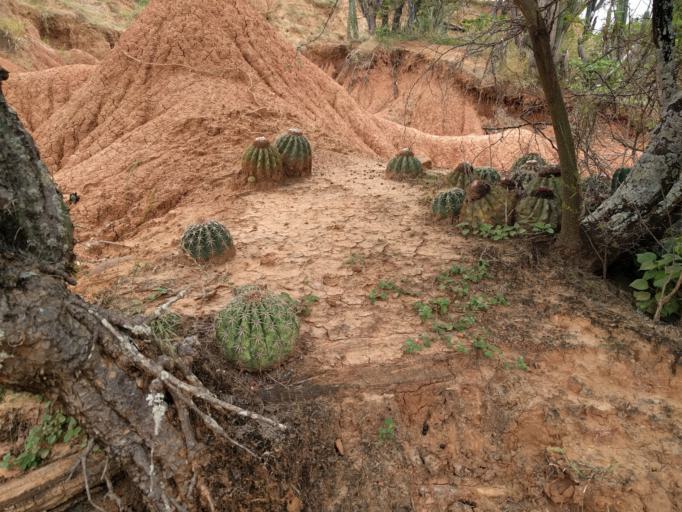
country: CO
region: Huila
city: Villavieja
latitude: 3.2301
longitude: -75.1694
